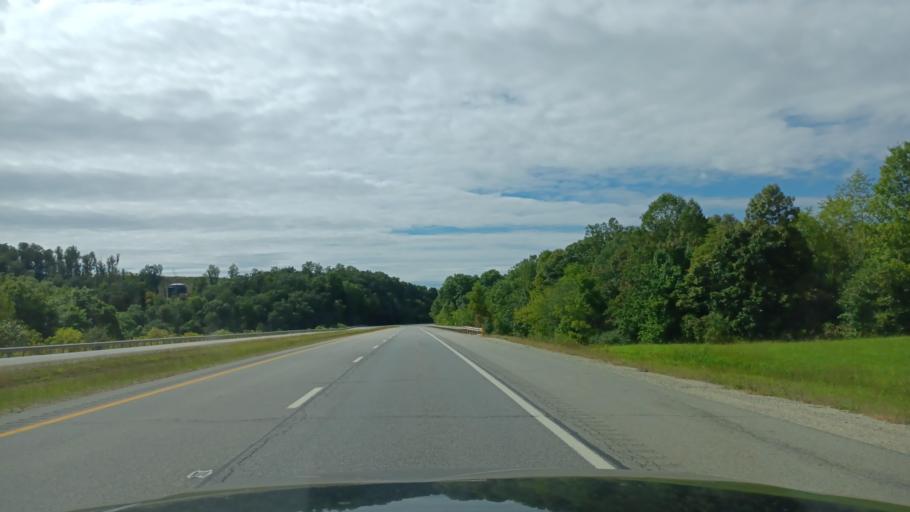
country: US
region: West Virginia
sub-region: Ritchie County
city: Pennsboro
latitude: 39.2708
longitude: -80.8944
